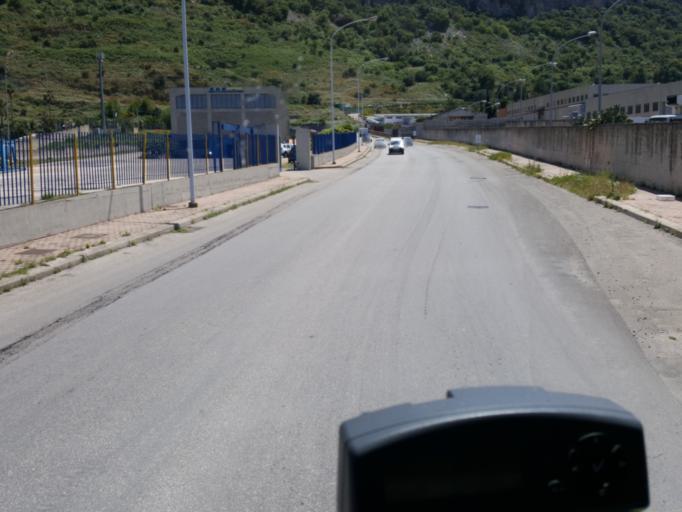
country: IT
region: Sicily
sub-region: Palermo
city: Carini
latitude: 38.1518
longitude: 13.2067
